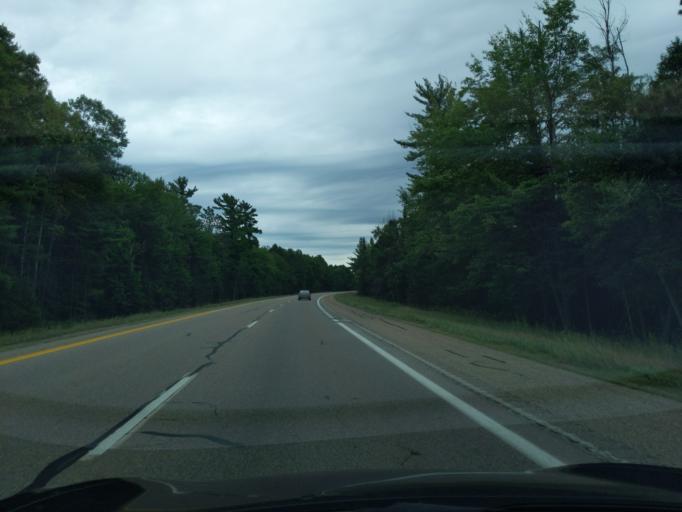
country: US
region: Michigan
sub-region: Roscommon County
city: Houghton Lake
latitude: 44.2274
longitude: -84.7984
